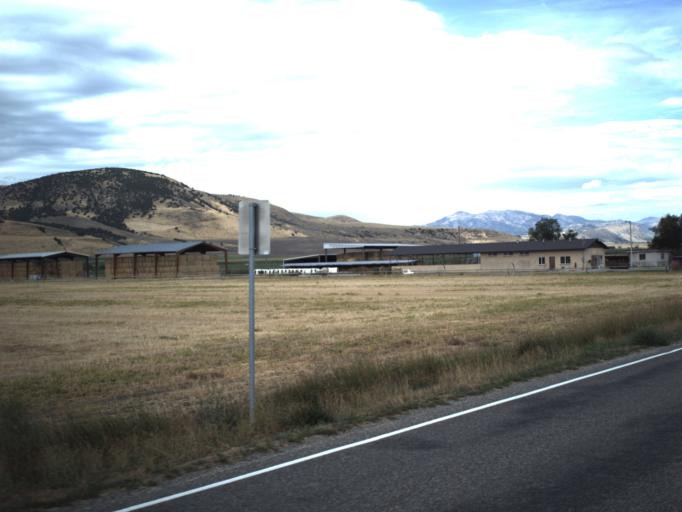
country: US
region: Utah
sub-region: Cache County
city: Lewiston
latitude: 41.9773
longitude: -111.9542
